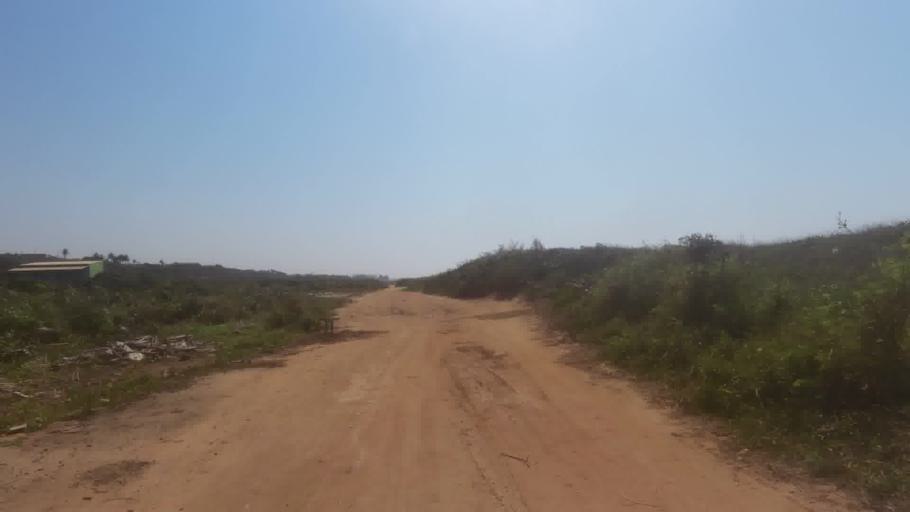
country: BR
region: Espirito Santo
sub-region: Marataizes
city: Marataizes
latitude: -21.0875
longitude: -40.8425
